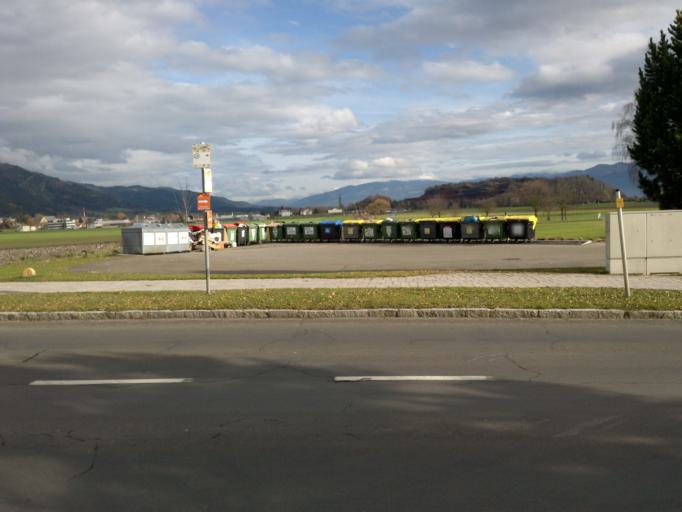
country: AT
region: Styria
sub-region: Politischer Bezirk Murtal
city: Fohnsdorf
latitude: 47.1991
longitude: 14.6640
